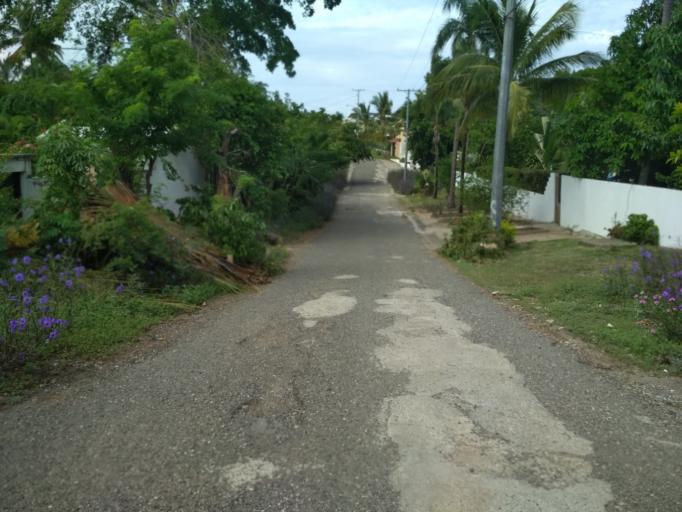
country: DO
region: Puerto Plata
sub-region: Puerto Plata
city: Puerto Plata
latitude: 19.8090
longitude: -70.7083
